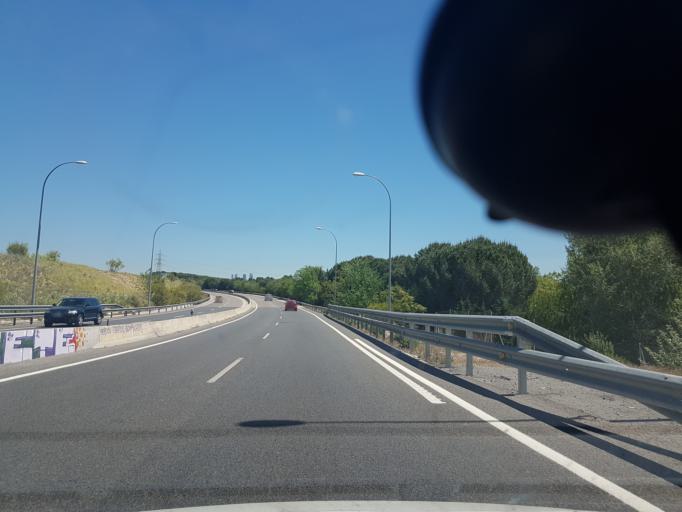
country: ES
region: Madrid
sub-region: Provincia de Madrid
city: Pozuelo de Alarcon
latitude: 40.4406
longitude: -3.7767
